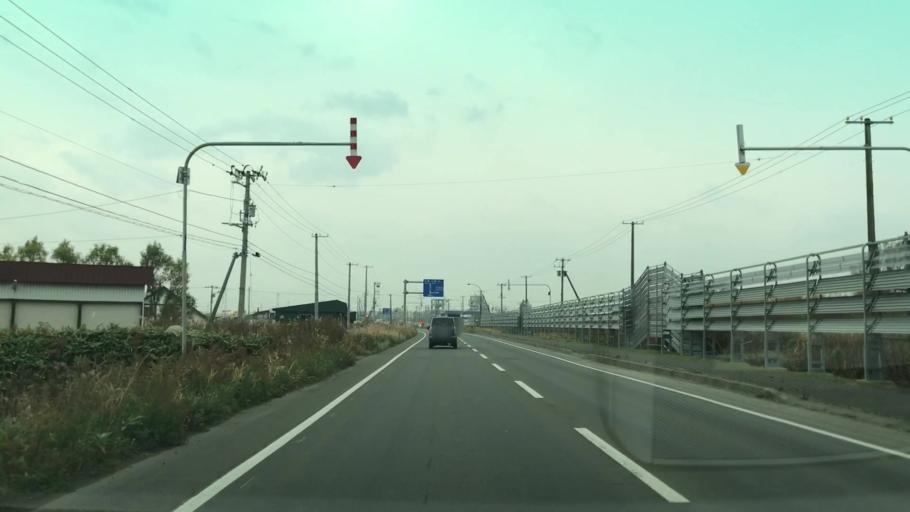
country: JP
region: Hokkaido
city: Ishikari
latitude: 43.2190
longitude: 141.3400
